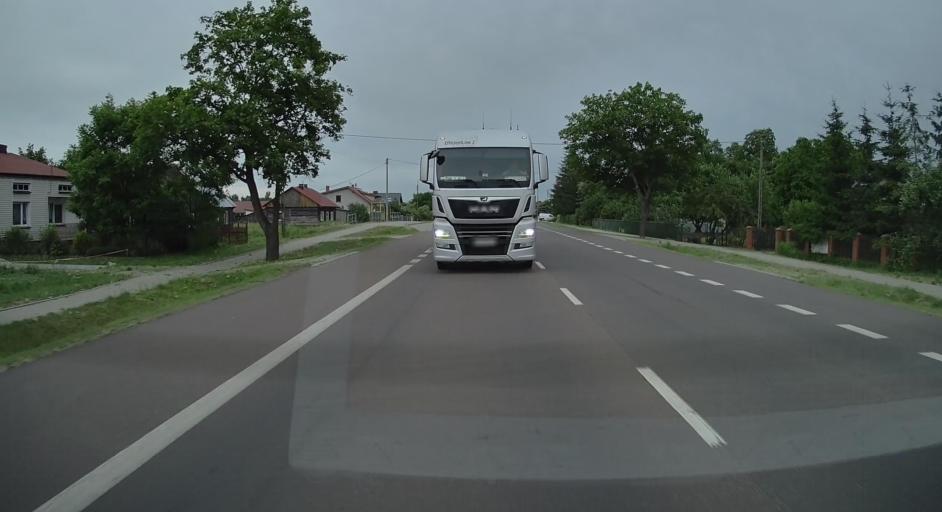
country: PL
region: Lublin Voivodeship
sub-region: Powiat bialski
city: Zalesie
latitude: 52.0374
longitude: 23.4815
